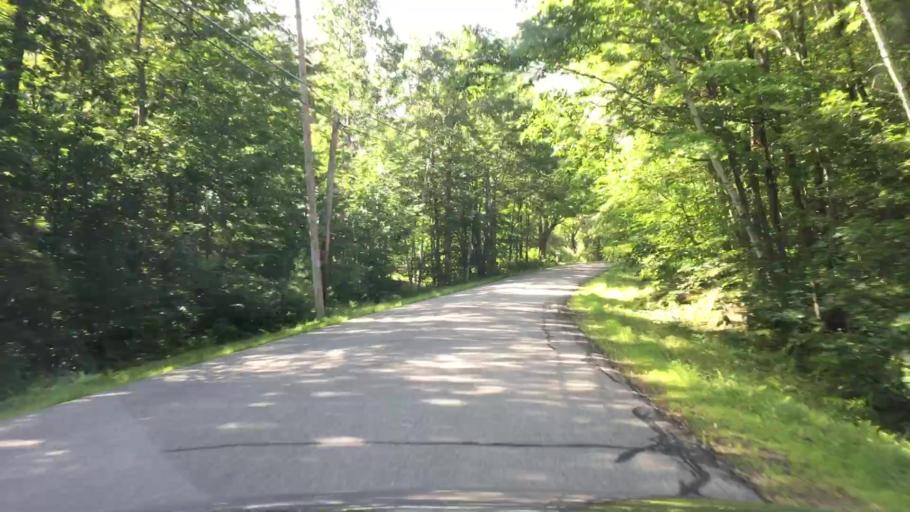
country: US
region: New Hampshire
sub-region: Grafton County
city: Ashland
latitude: 43.7140
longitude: -71.6299
